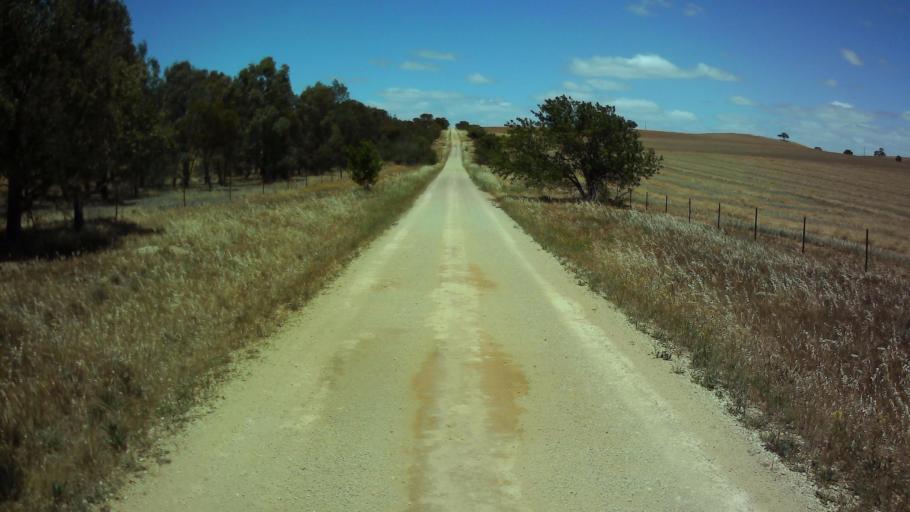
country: AU
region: New South Wales
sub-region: Weddin
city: Grenfell
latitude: -33.9427
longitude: 148.3709
